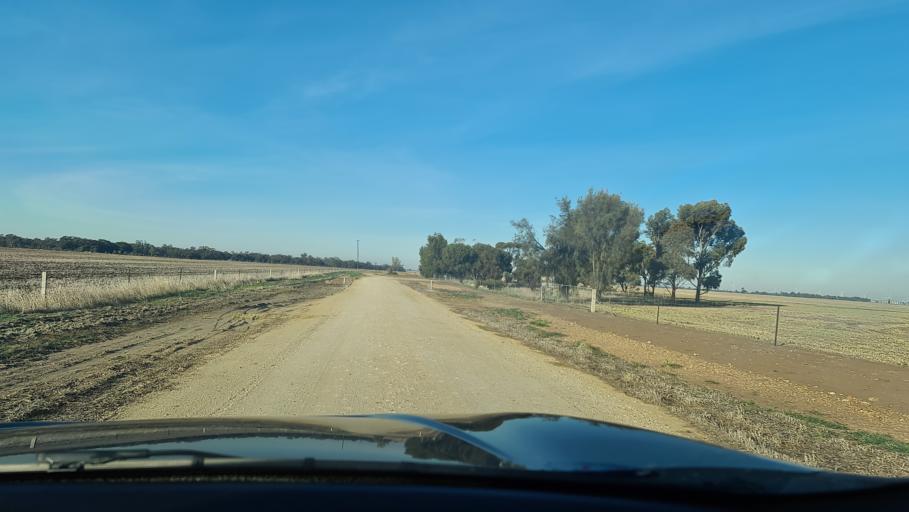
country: AU
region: Victoria
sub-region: Horsham
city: Horsham
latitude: -36.3639
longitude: 142.3957
